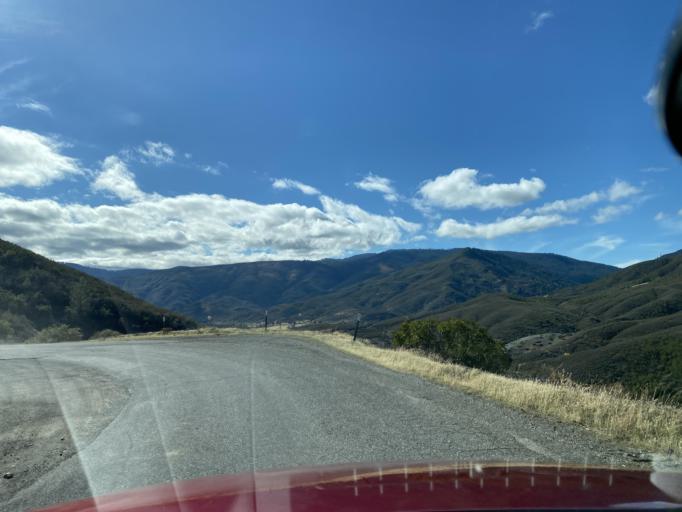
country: US
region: California
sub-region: Lake County
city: Lucerne
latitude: 39.3673
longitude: -122.6522
